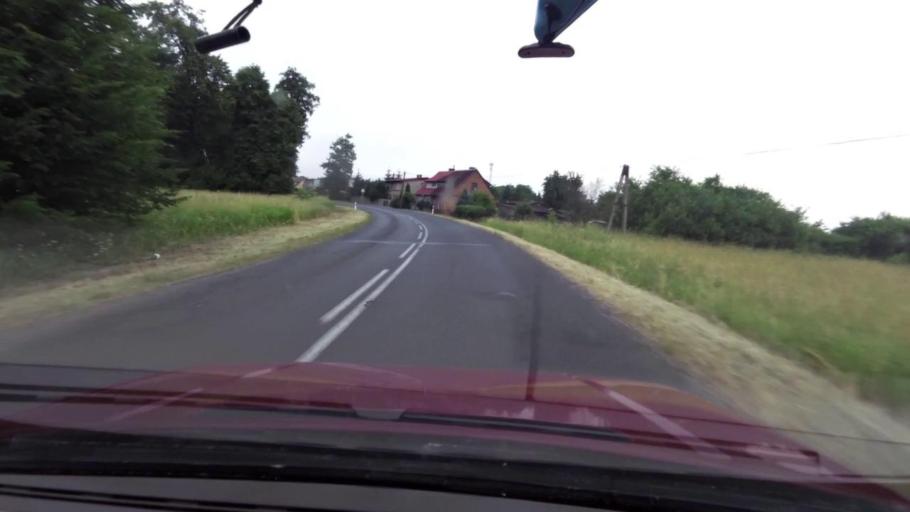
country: PL
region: West Pomeranian Voivodeship
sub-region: Powiat koszalinski
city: Sianow
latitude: 54.1606
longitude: 16.4497
